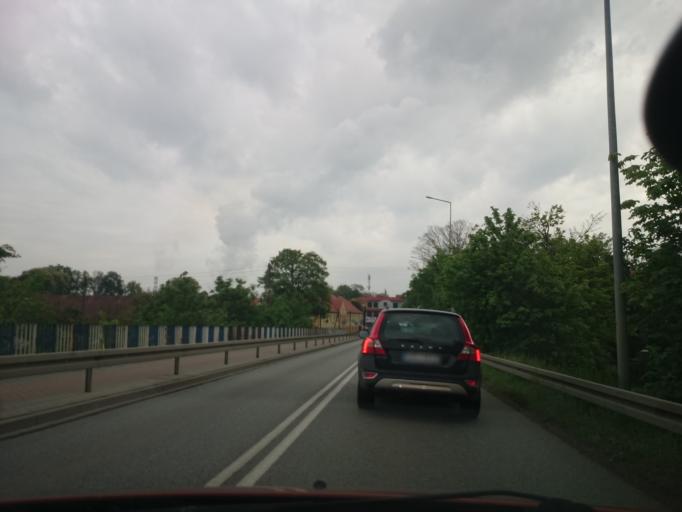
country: PL
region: Opole Voivodeship
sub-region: Powiat opolski
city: Czarnowasy
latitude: 50.7184
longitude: 17.9027
